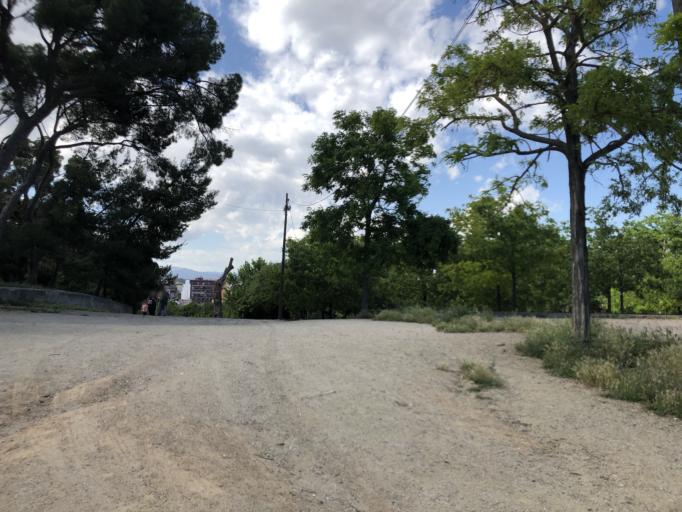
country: ES
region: Catalonia
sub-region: Provincia de Barcelona
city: Rubi
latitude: 41.4925
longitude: 2.0415
